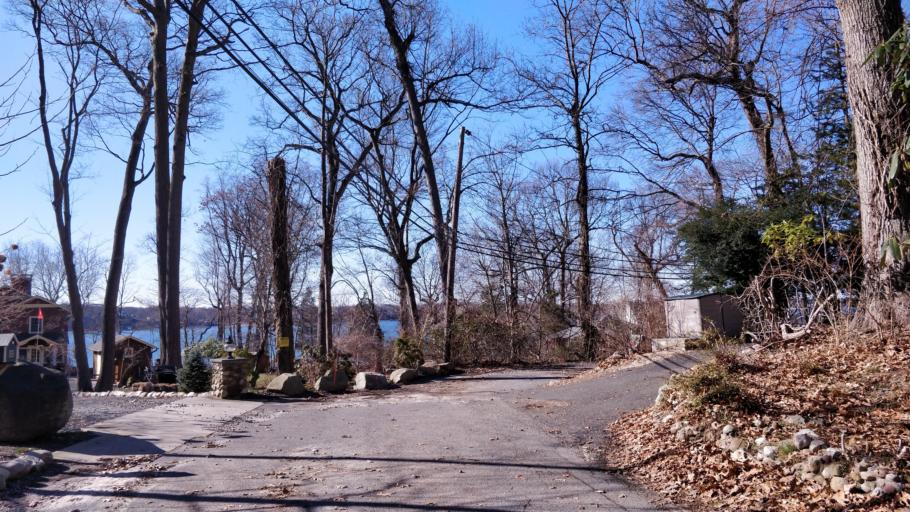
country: US
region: New York
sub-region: Suffolk County
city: Port Jefferson
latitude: 40.9607
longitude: -73.0730
